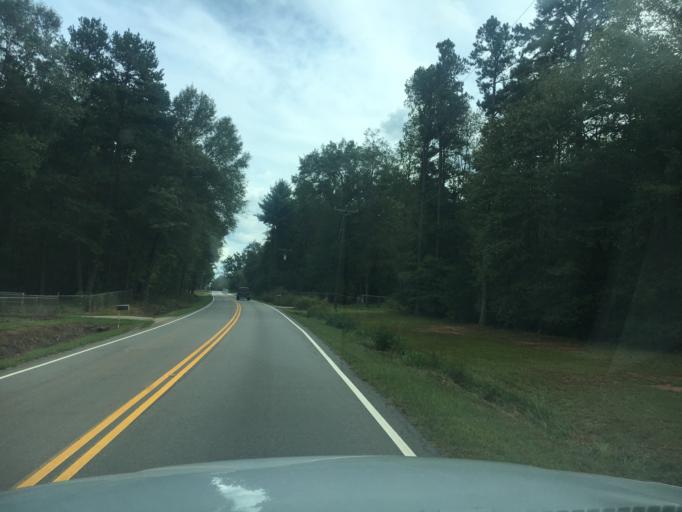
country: US
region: South Carolina
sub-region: Spartanburg County
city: Wellford
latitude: 34.9230
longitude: -82.0625
